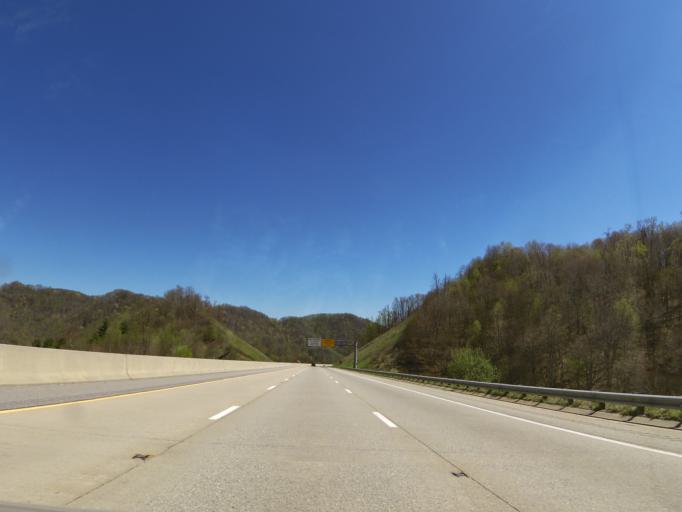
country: US
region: North Carolina
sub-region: Madison County
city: Mars Hill
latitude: 35.9375
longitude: -82.5603
